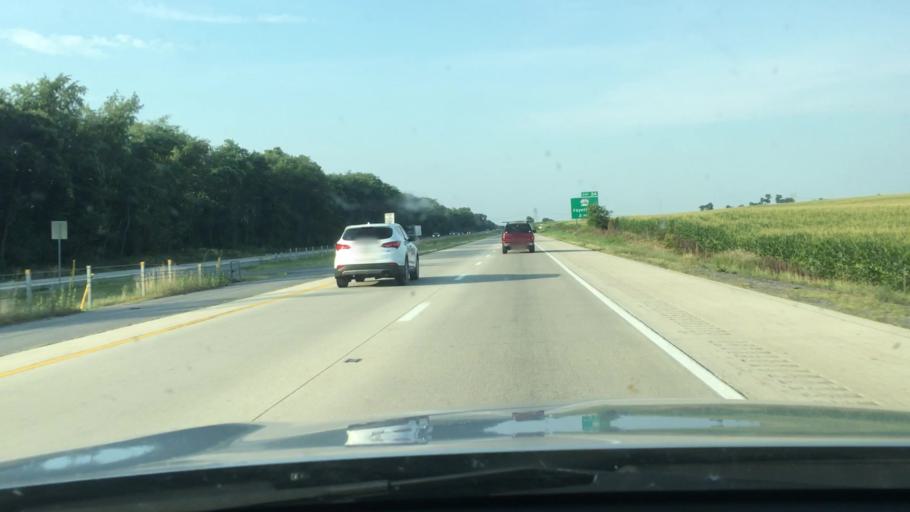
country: US
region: Pennsylvania
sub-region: Franklin County
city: Scotland
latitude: 39.9924
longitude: -77.5594
